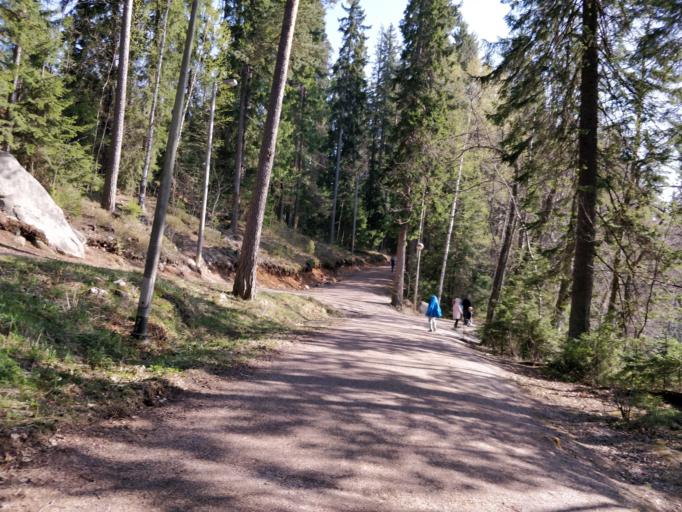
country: FI
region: Uusimaa
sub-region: Helsinki
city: Vantaa
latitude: 60.3132
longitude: 25.1179
